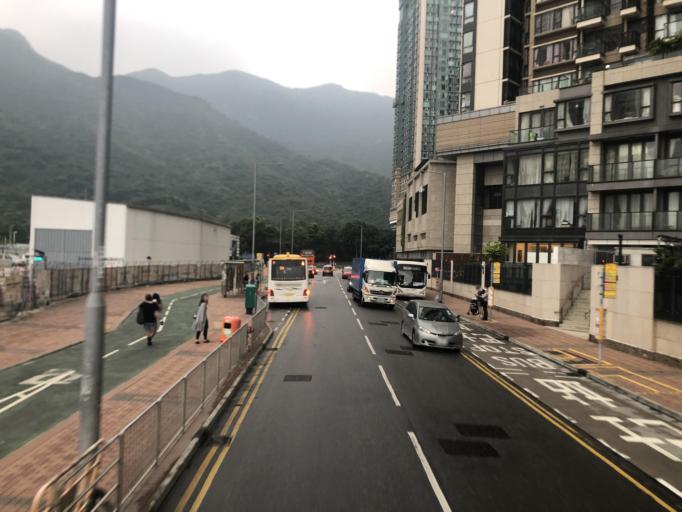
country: HK
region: Tuen Mun
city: Tuen Mun
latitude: 22.2960
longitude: 113.9519
